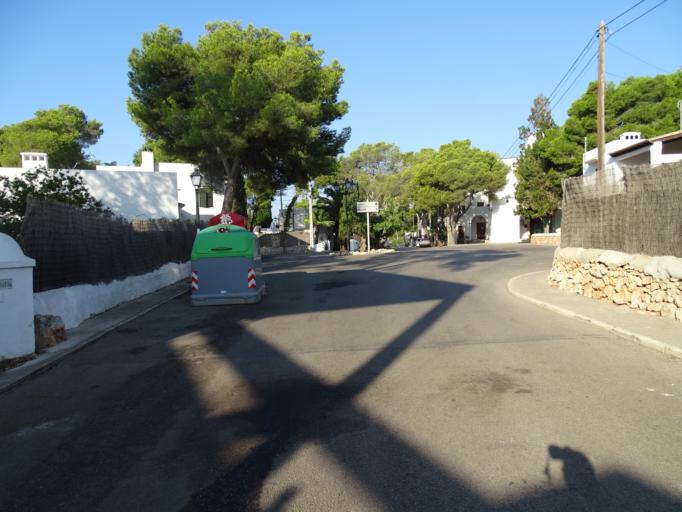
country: ES
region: Balearic Islands
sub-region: Illes Balears
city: Santanyi
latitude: 39.3707
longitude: 3.2287
